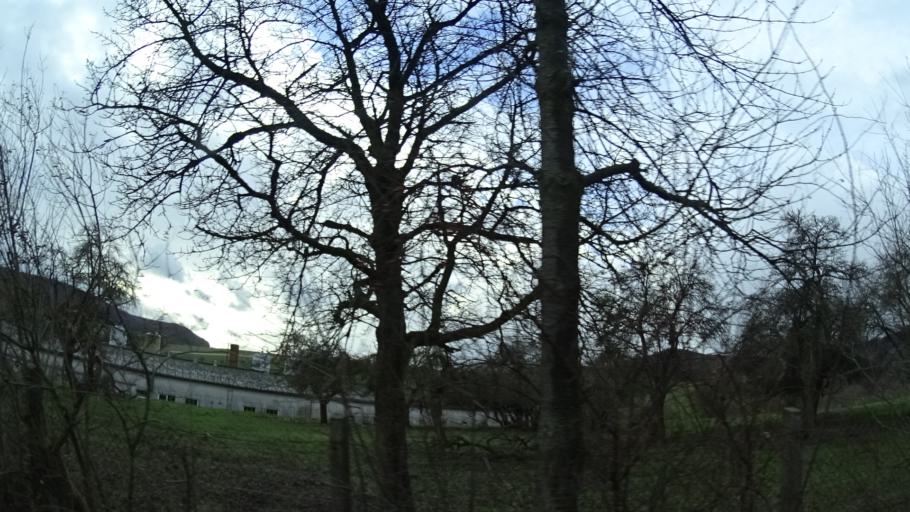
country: DE
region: Thuringia
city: Stepfershausen
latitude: 50.5578
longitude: 10.2801
